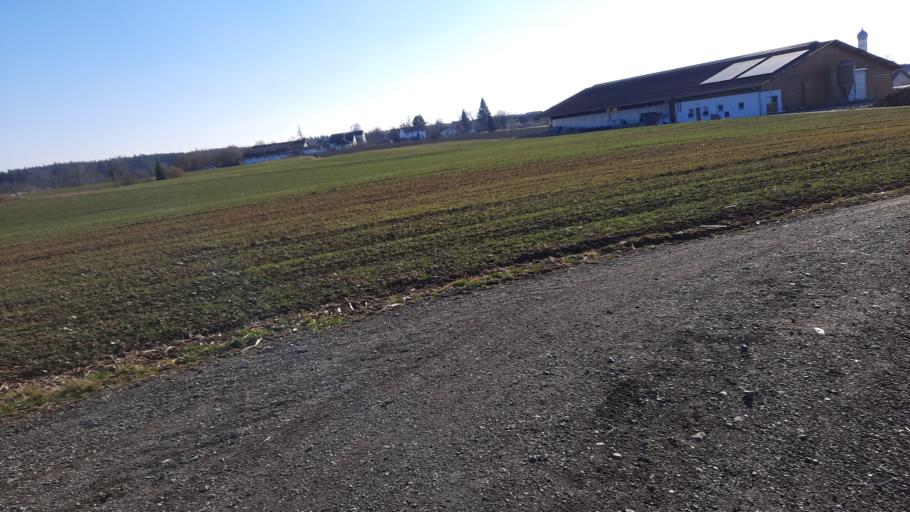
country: DE
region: Bavaria
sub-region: Upper Bavaria
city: Oberpframmern
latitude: 48.0248
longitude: 11.8195
